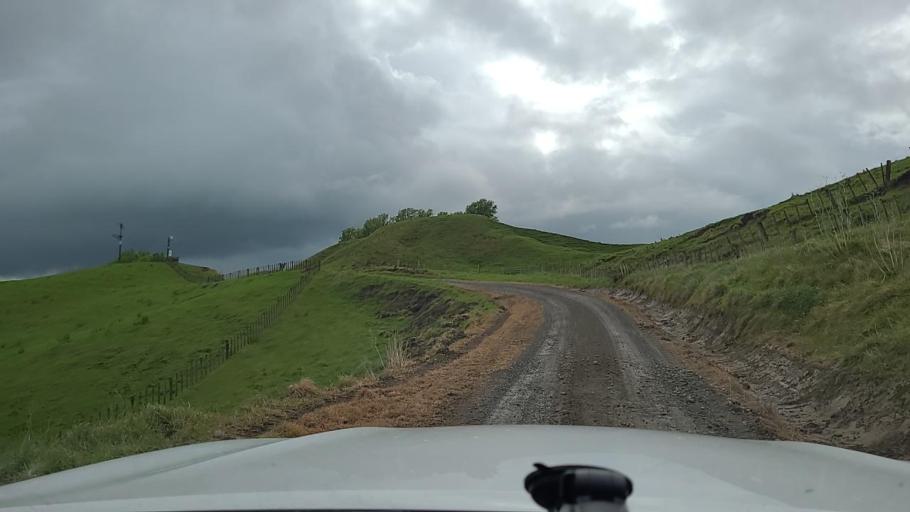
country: NZ
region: Gisborne
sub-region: Gisborne District
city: Gisborne
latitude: -38.4366
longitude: 177.7128
